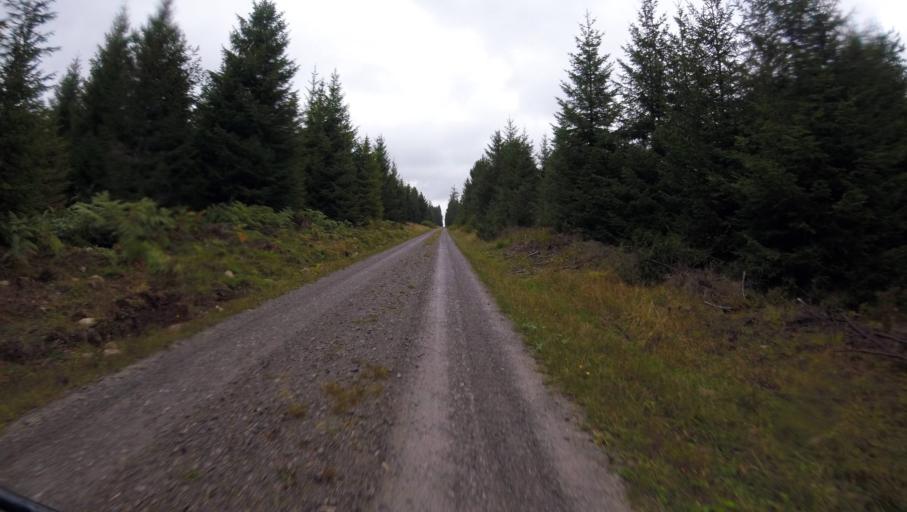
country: DE
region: Baden-Wuerttemberg
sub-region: Karlsruhe Region
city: Enzklosterle
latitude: 48.6859
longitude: 8.4184
